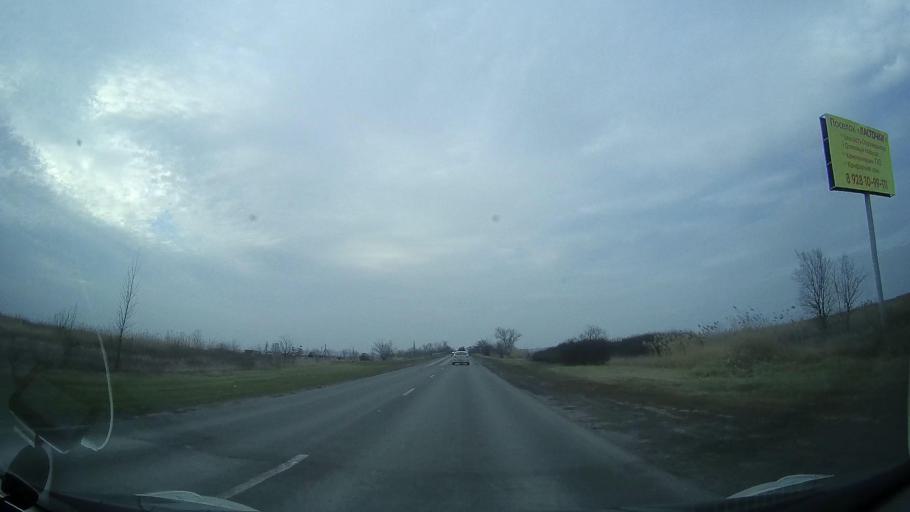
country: RU
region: Rostov
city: Ol'ginskaya
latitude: 47.2033
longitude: 39.9294
